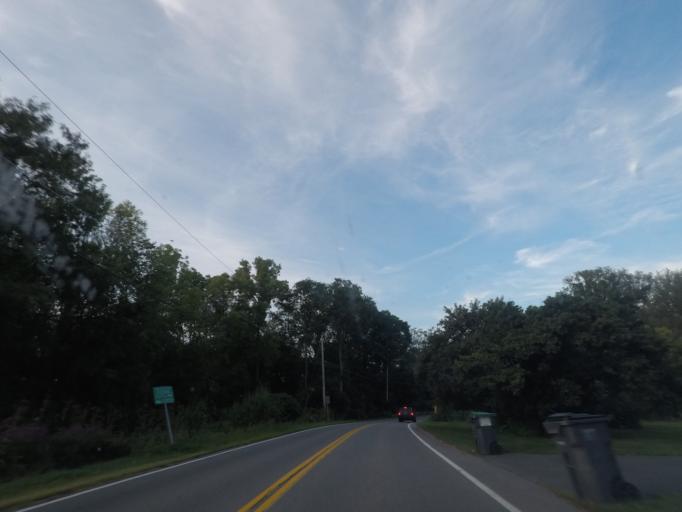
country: US
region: New York
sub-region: Schenectady County
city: Niskayuna
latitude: 42.7780
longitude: -73.7924
